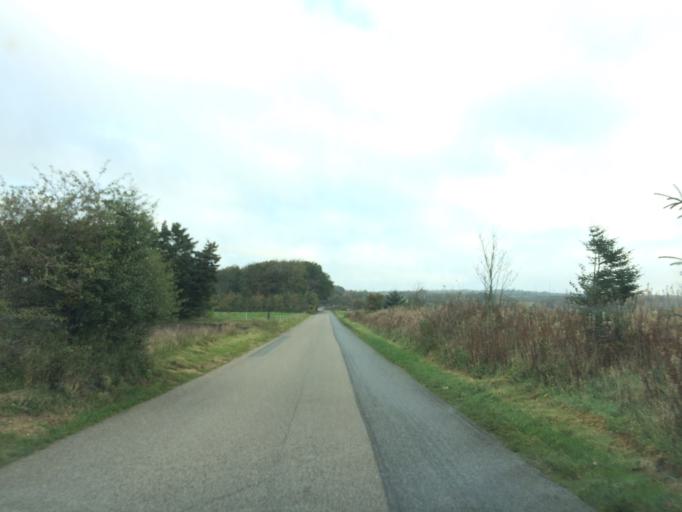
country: DK
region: Central Jutland
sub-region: Holstebro Kommune
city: Holstebro
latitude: 56.3475
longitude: 8.5109
